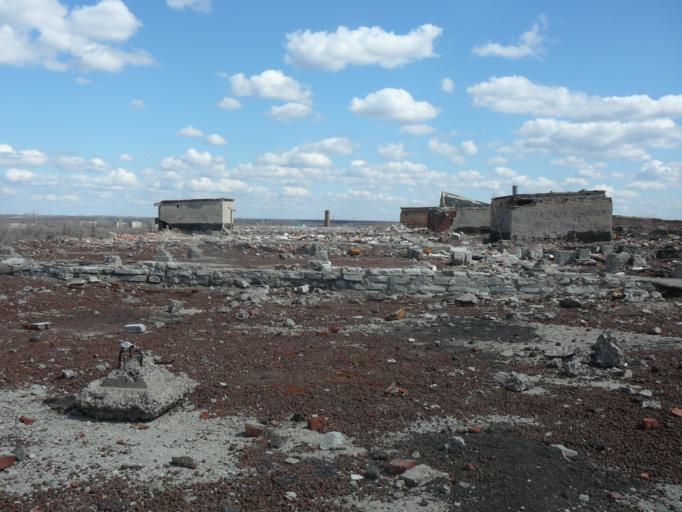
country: RU
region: Saratov
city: Privolzhskiy
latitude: 51.4118
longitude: 46.0519
